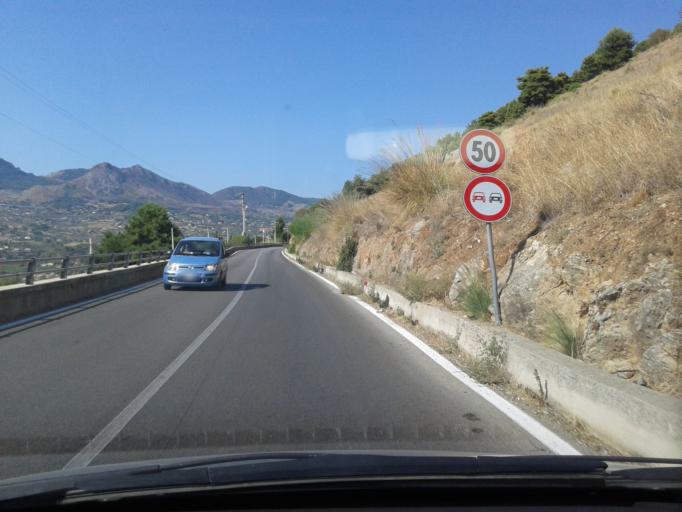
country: IT
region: Sicily
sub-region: Palermo
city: Cannizzaro-Favara
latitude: 38.0589
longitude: 13.2596
